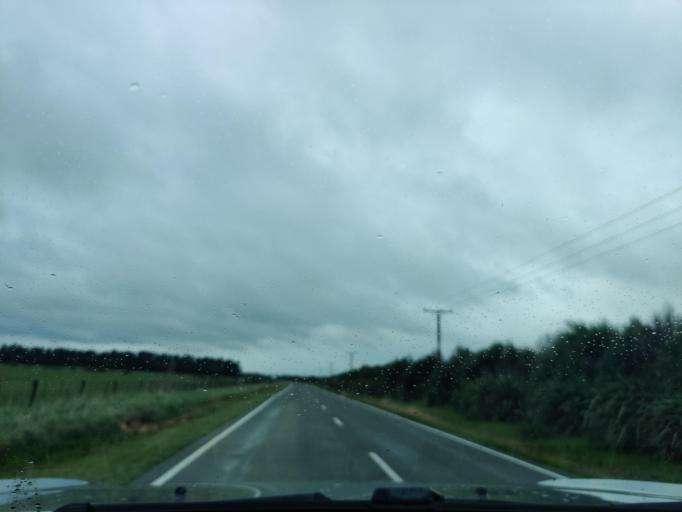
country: NZ
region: Hawke's Bay
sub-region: Hastings District
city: Hastings
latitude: -40.0076
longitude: 176.3840
